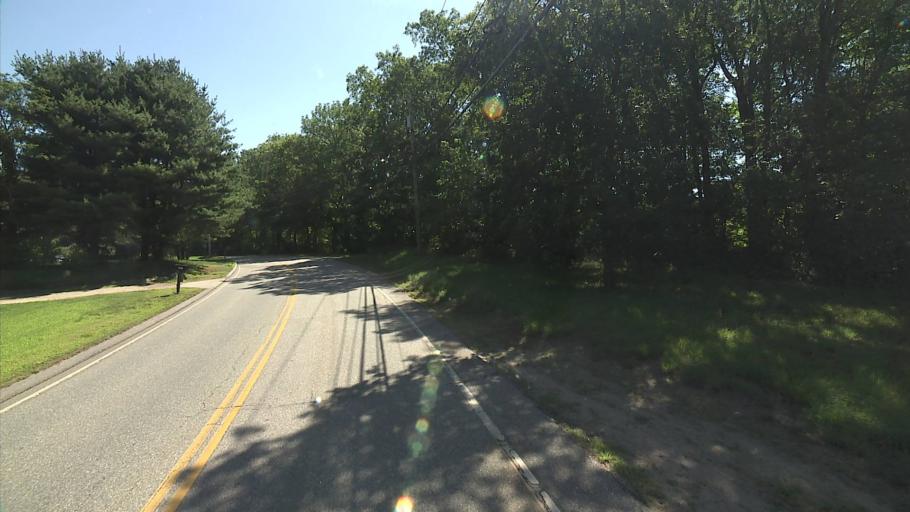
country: US
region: Connecticut
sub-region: New London County
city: Colchester
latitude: 41.5956
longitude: -72.2879
